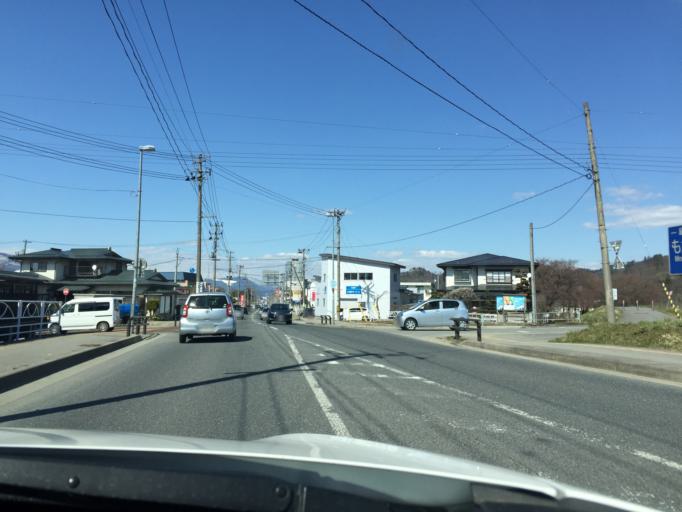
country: JP
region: Yamagata
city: Nagai
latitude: 38.0964
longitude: 140.0418
